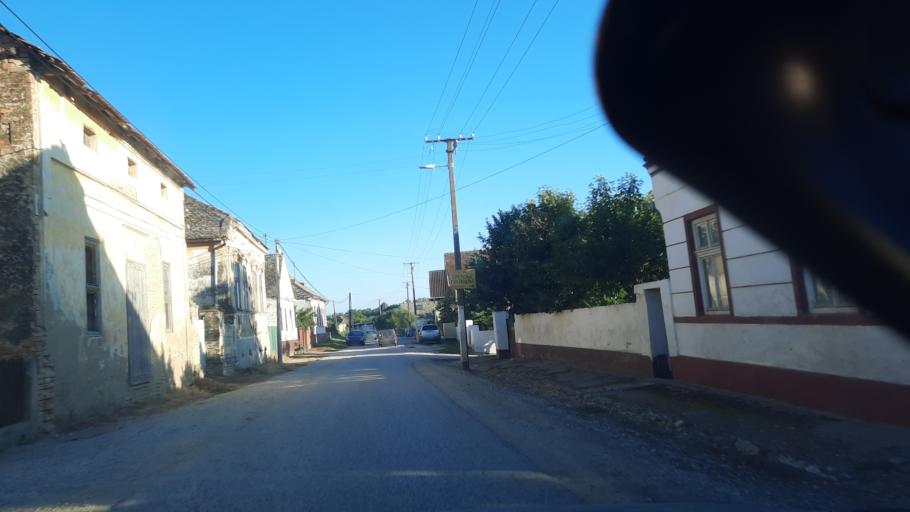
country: RS
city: Cortanovci
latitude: 45.1162
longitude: 19.9458
